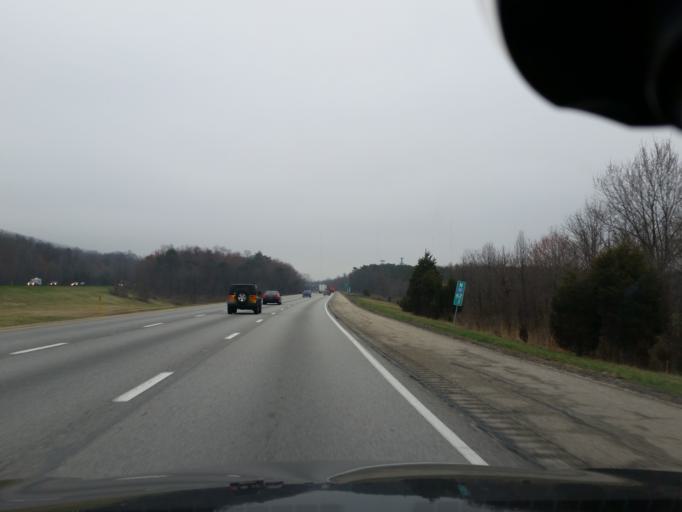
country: US
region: Pennsylvania
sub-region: Cumberland County
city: Enola
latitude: 40.3017
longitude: -76.9689
